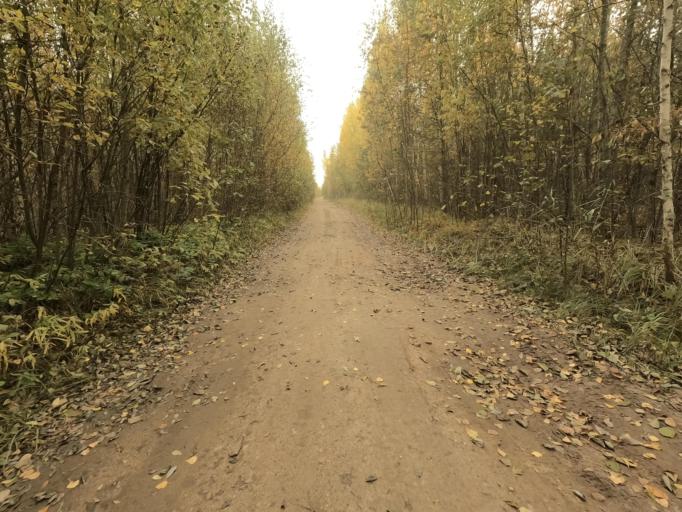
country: RU
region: Novgorod
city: Pankovka
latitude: 58.8769
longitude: 30.8671
